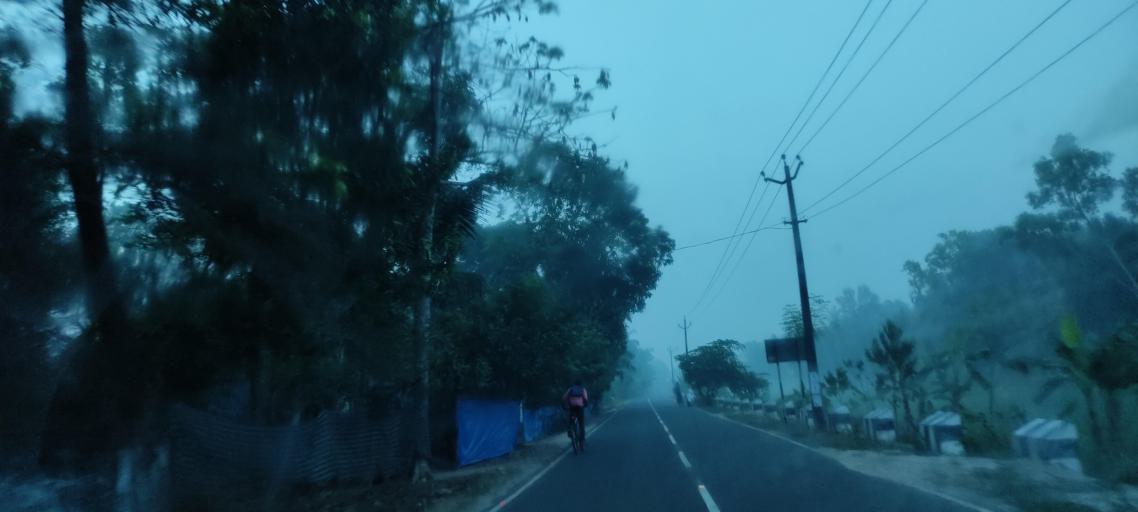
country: IN
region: Kerala
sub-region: Alappuzha
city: Alleppey
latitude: 9.5804
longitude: 76.3319
